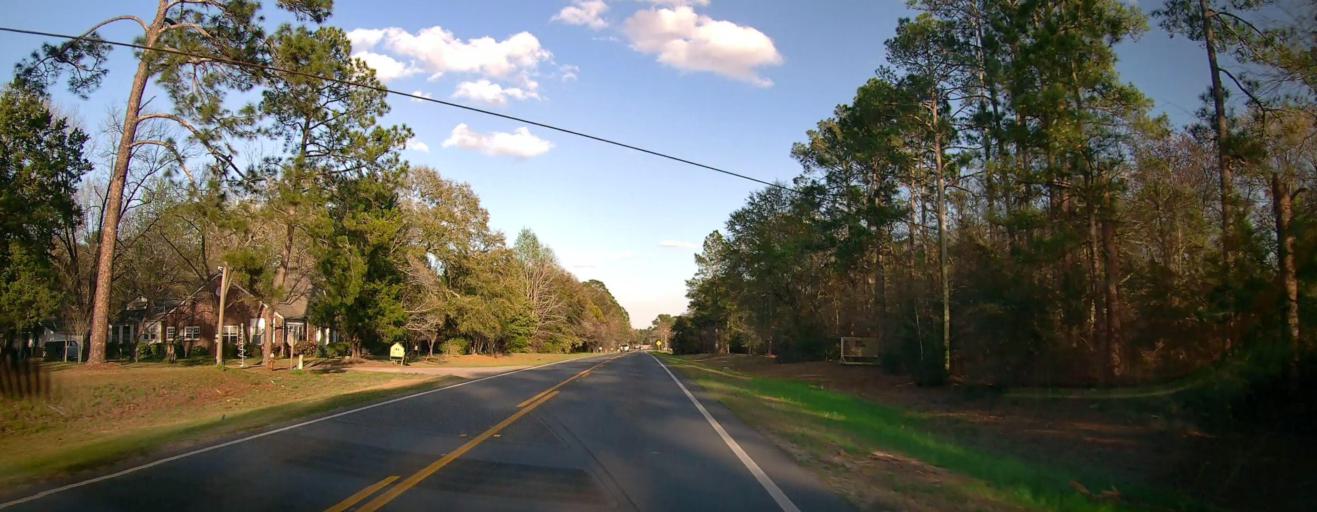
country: US
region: Georgia
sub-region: Evans County
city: Claxton
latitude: 32.1616
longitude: -81.8896
